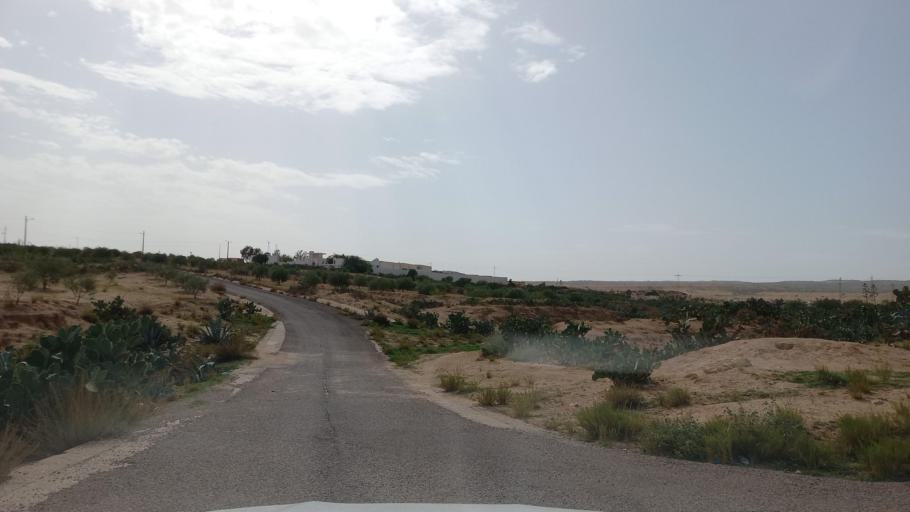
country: TN
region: Al Qasrayn
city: Kasserine
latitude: 35.2996
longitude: 8.9534
